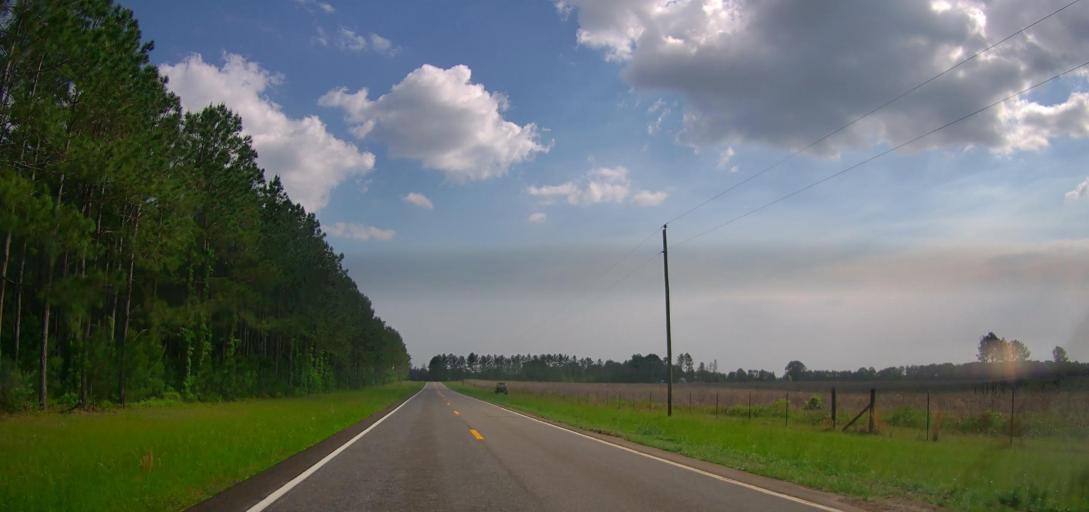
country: US
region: Georgia
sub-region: Laurens County
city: East Dublin
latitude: 32.6405
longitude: -82.8949
